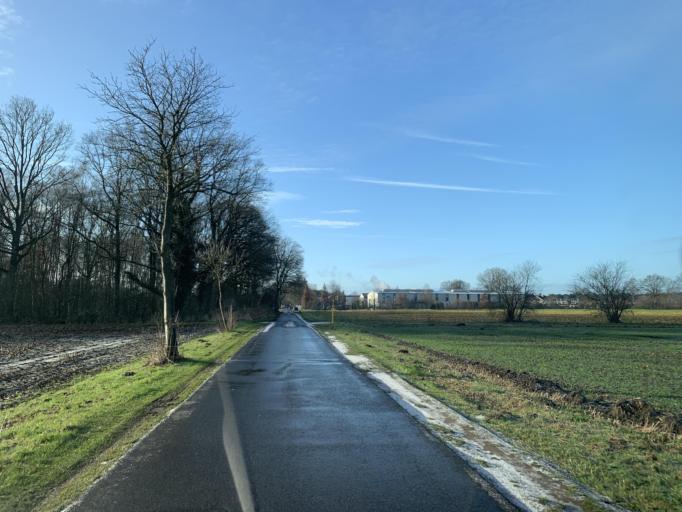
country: DE
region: North Rhine-Westphalia
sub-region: Regierungsbezirk Munster
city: Dulmen
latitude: 51.8045
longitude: 7.2732
